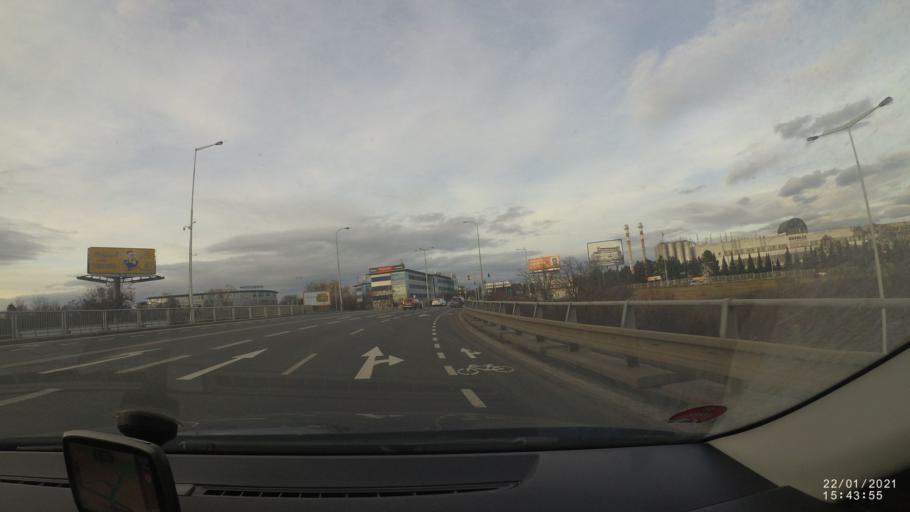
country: CZ
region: Praha
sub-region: Praha 1
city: Mala Strana
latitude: 50.0552
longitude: 14.3394
